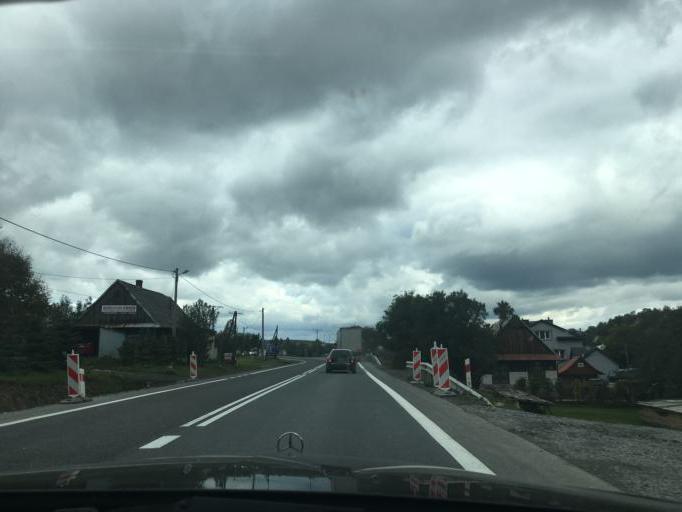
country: PL
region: Subcarpathian Voivodeship
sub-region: Powiat krosnienski
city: Dukla
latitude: 49.5371
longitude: 21.6942
